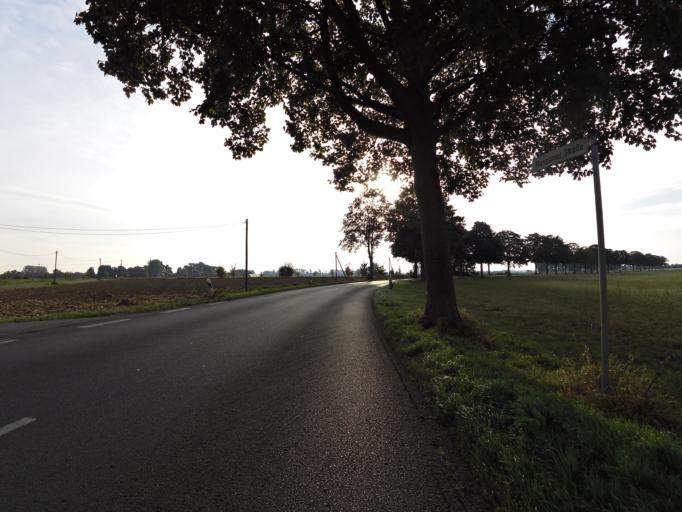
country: DE
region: North Rhine-Westphalia
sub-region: Regierungsbezirk Dusseldorf
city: Hamminkeln
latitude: 51.7941
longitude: 6.5567
